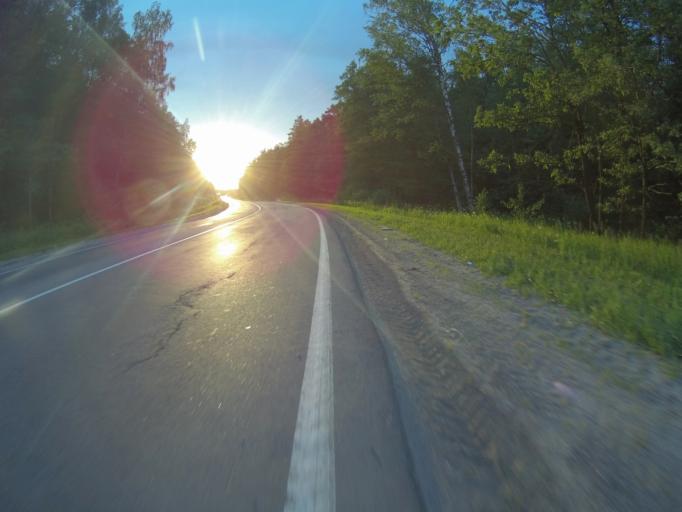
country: RU
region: Vladimir
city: Kommunar
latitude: 56.0596
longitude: 40.5150
